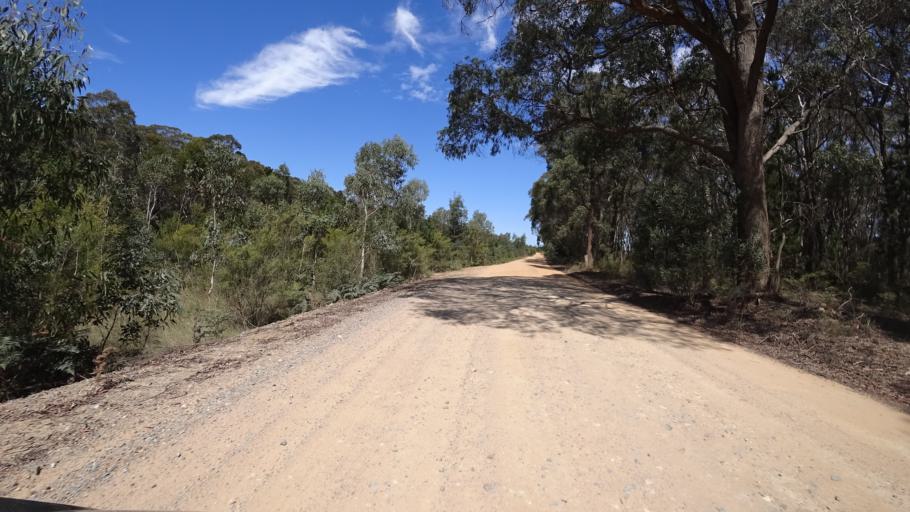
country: AU
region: New South Wales
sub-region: Lithgow
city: Lithgow
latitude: -33.3448
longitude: 150.2552
